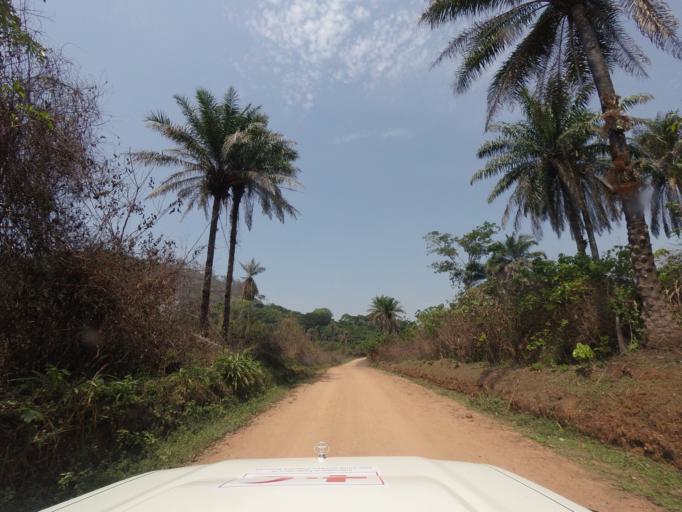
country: LR
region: Lofa
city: Voinjama
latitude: 8.4401
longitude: -9.7010
